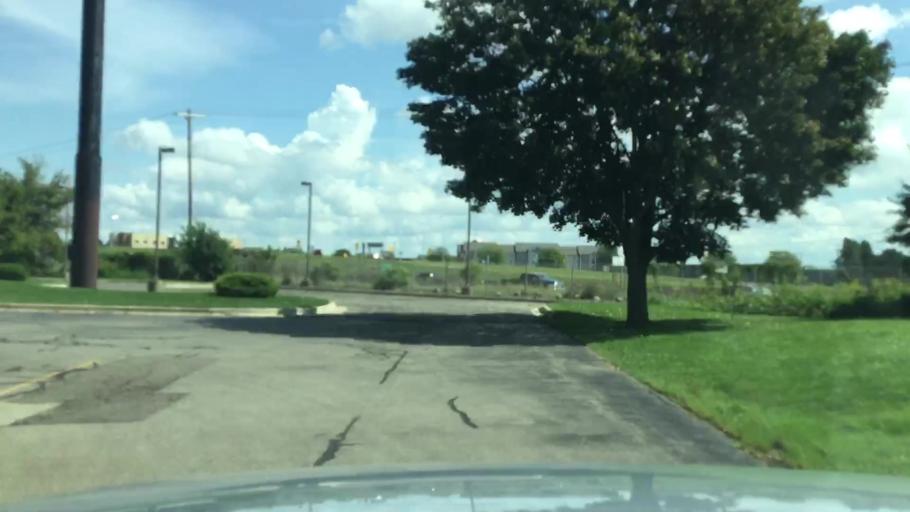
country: US
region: Michigan
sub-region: Kalamazoo County
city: Eastwood
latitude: 42.2577
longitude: -85.5348
